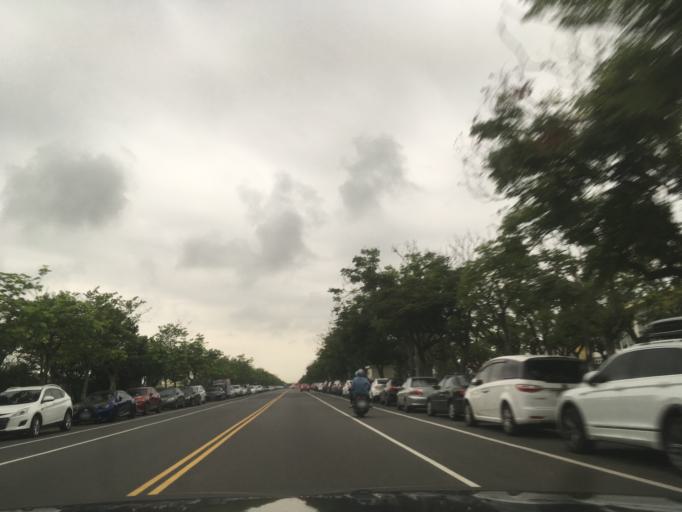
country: TW
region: Taiwan
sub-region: Yilan
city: Yilan
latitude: 24.7389
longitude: 121.7573
